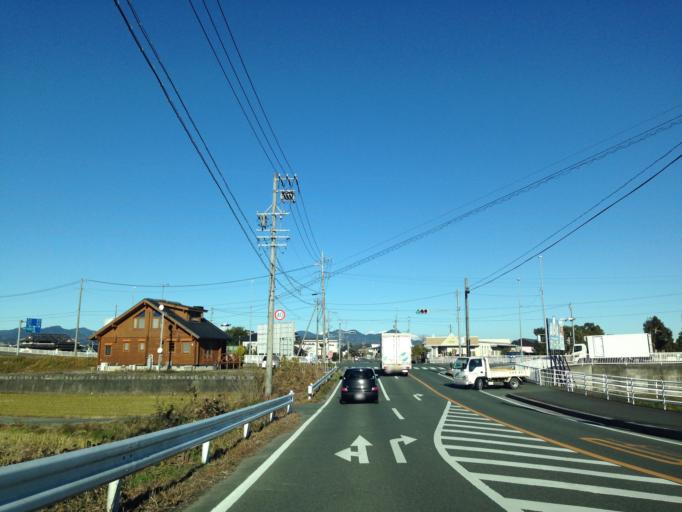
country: JP
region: Shizuoka
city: Kakegawa
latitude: 34.7593
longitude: 137.9711
